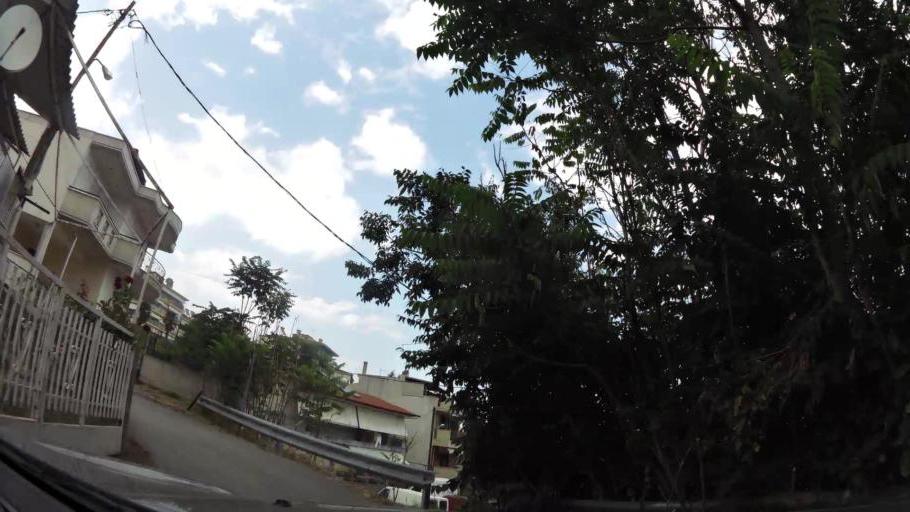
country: GR
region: Central Macedonia
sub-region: Nomos Imathias
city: Veroia
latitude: 40.5197
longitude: 22.2087
